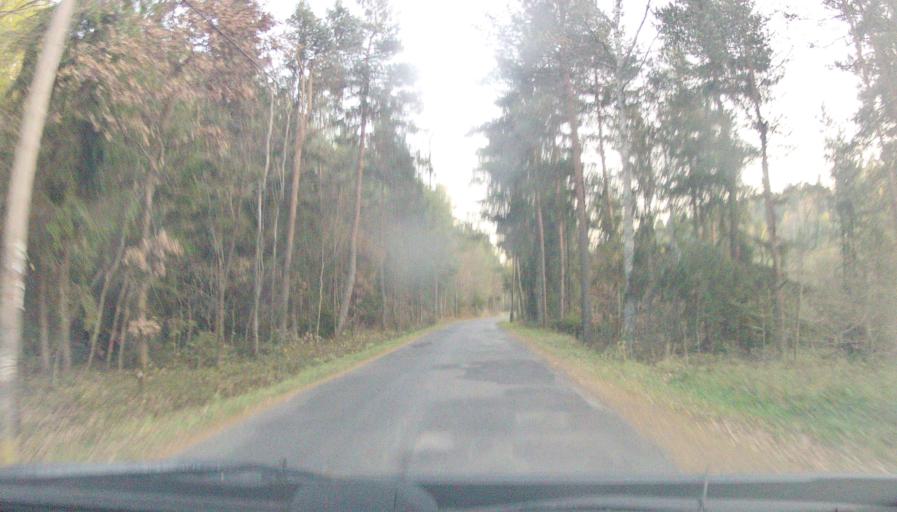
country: PL
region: Lesser Poland Voivodeship
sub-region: Powiat suski
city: Krzeszow
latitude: 49.7540
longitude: 19.4602
